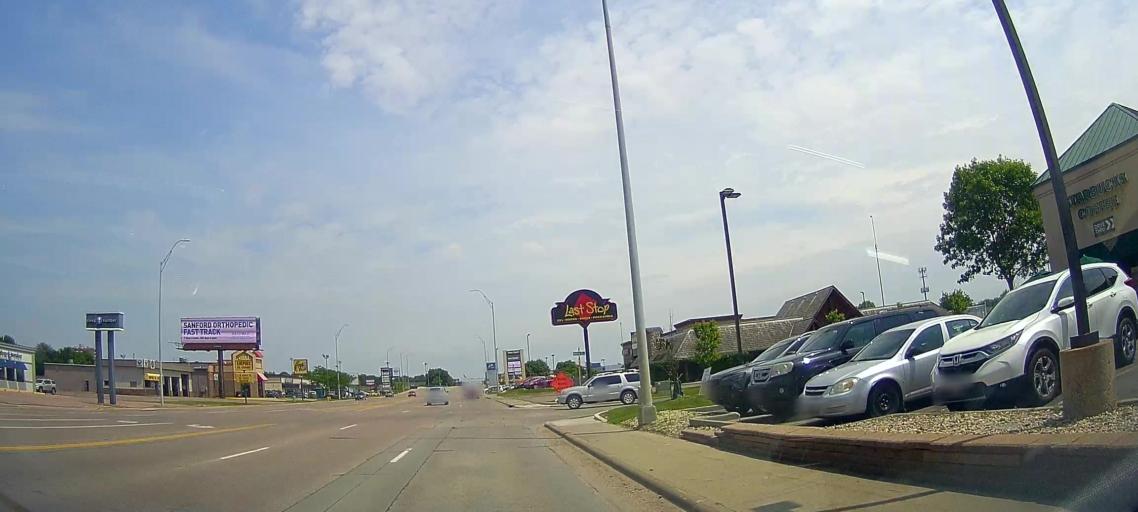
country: US
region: South Dakota
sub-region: Minnehaha County
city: Sioux Falls
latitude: 43.5147
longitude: -96.7701
